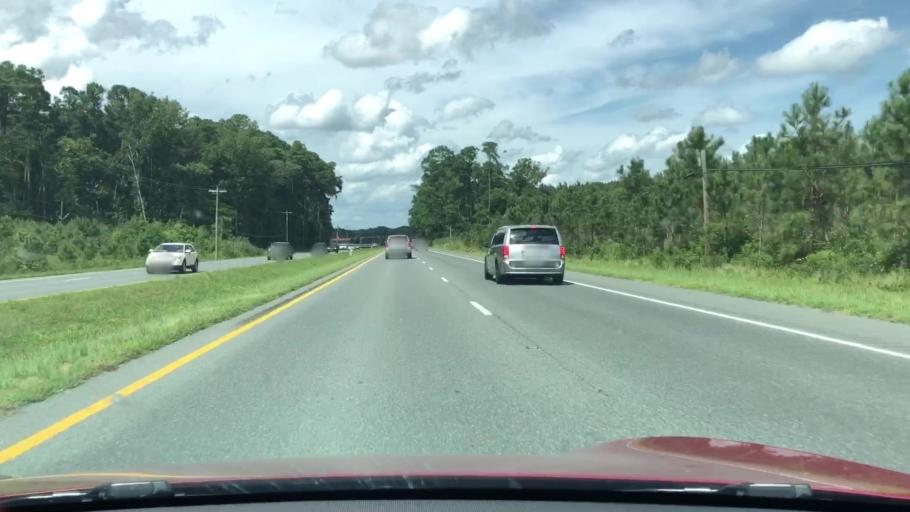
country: US
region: Virginia
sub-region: Accomack County
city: Wattsville
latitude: 37.9171
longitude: -75.5492
